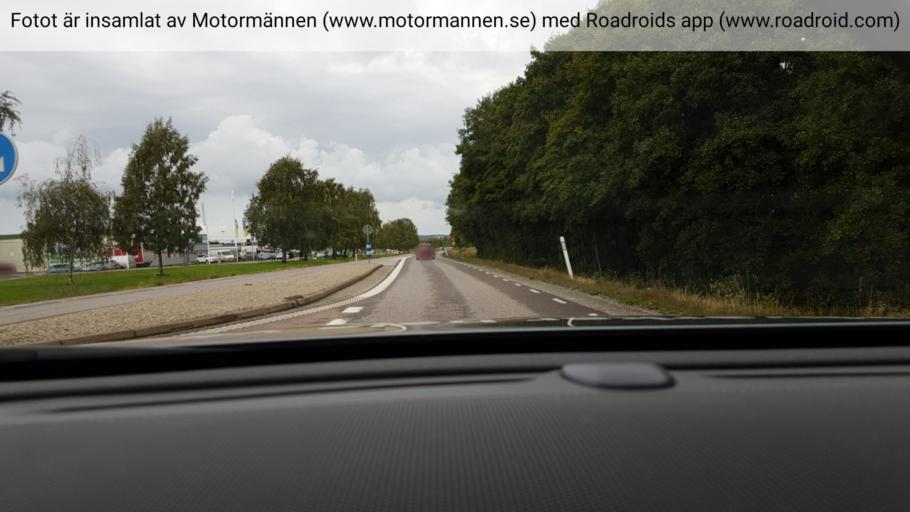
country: SE
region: Vaestra Goetaland
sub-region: Stenungsunds Kommun
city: Stenungsund
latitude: 58.0723
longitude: 11.8479
